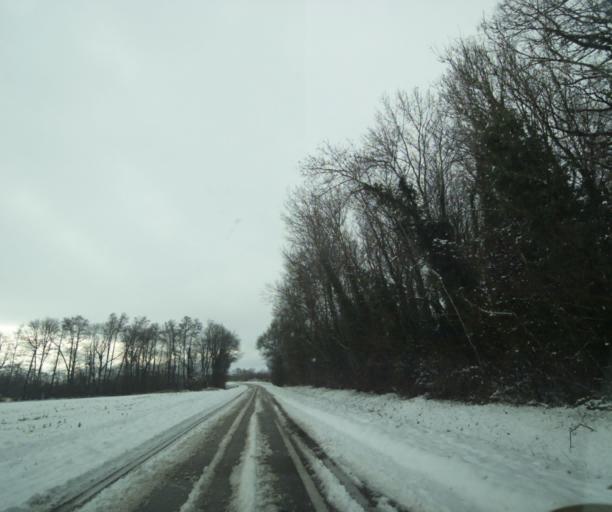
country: FR
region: Champagne-Ardenne
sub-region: Departement de la Haute-Marne
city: Montier-en-Der
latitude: 48.4751
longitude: 4.6642
